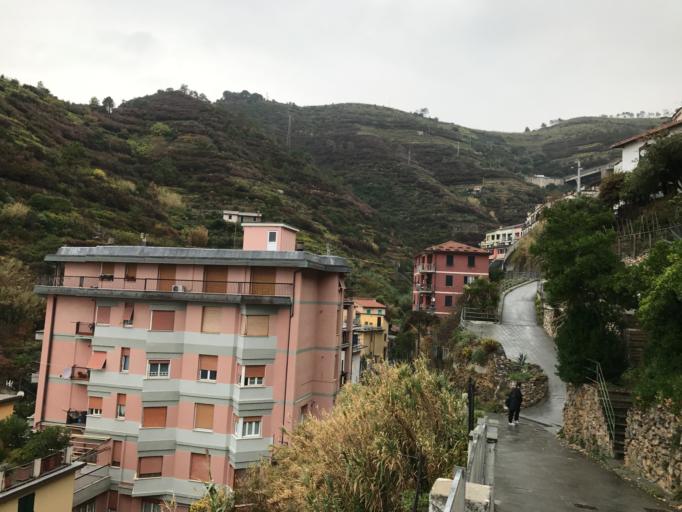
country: IT
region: Liguria
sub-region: Provincia di La Spezia
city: Riomaggiore
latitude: 44.1009
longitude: 9.7367
